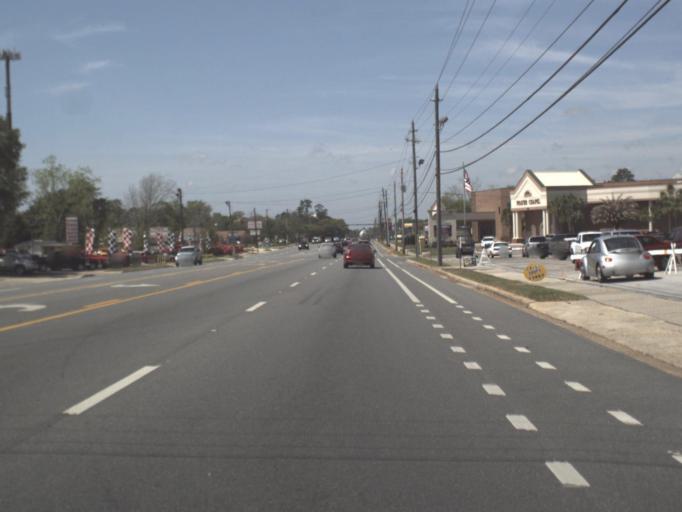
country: US
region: Florida
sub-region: Santa Rosa County
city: Pace
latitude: 30.6010
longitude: -87.1575
